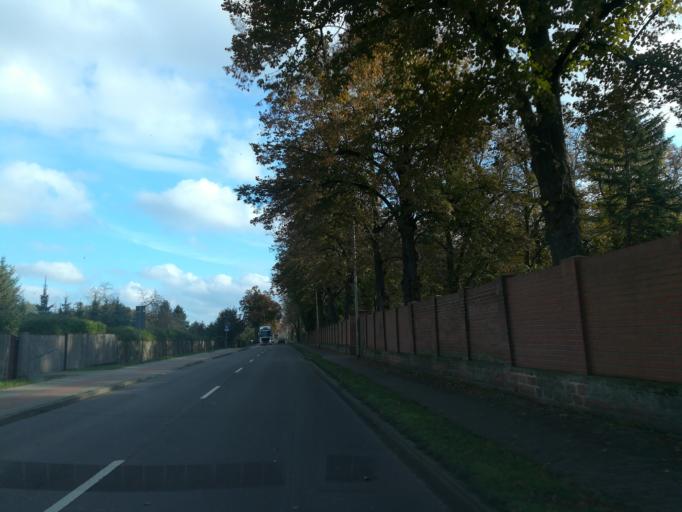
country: DE
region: Saxony-Anhalt
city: Haldensleben I
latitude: 52.2857
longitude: 11.4226
